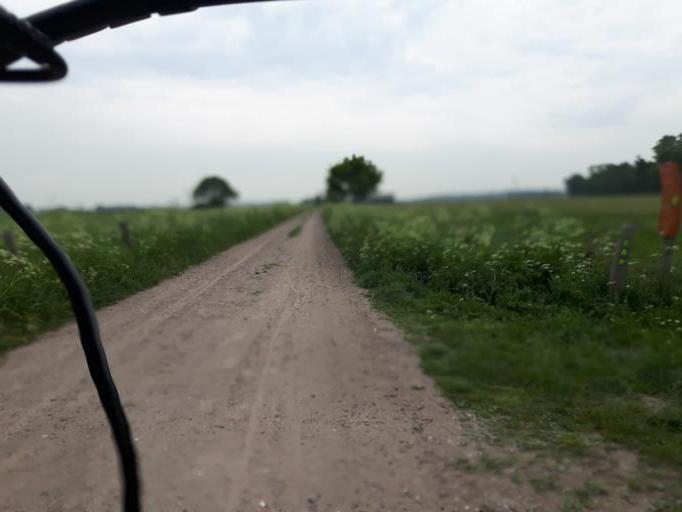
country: NL
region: North Brabant
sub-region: Gemeente Steenbergen
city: Welberg
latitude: 51.5558
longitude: 4.3228
